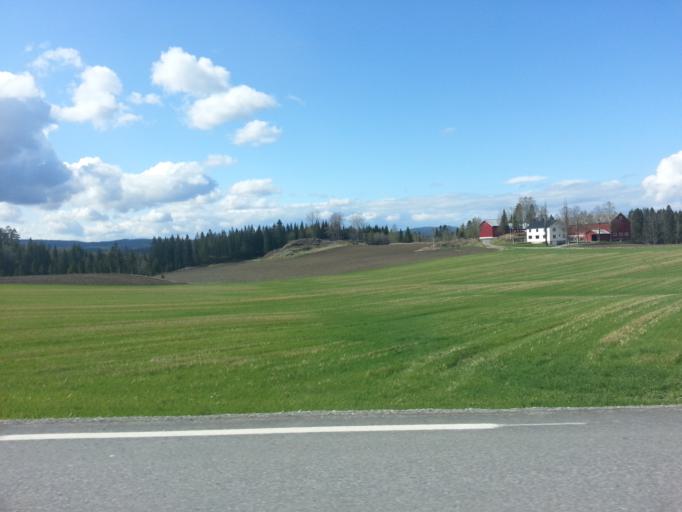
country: NO
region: Nord-Trondelag
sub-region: Levanger
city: Skogn
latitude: 63.6394
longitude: 11.2594
